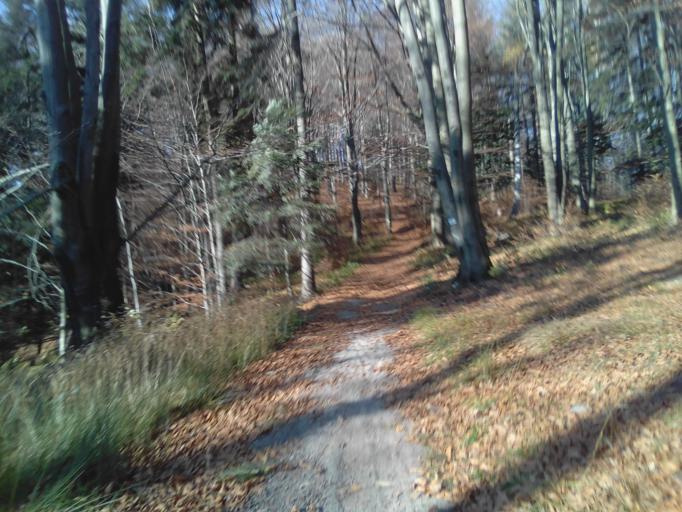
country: PL
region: Subcarpathian Voivodeship
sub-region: Powiat krosnienski
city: Leki
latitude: 49.8249
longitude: 21.6920
